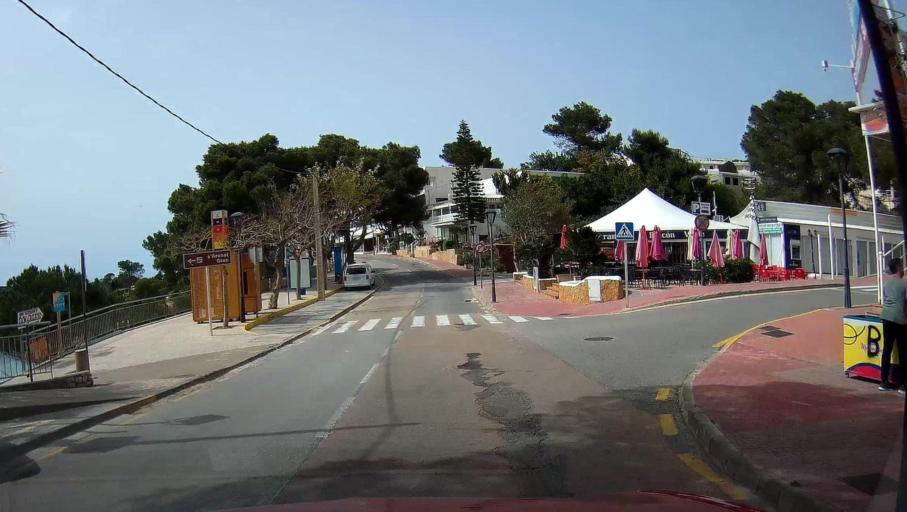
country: ES
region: Balearic Islands
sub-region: Illes Balears
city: Sant Joan de Labritja
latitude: 39.1102
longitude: 1.5180
